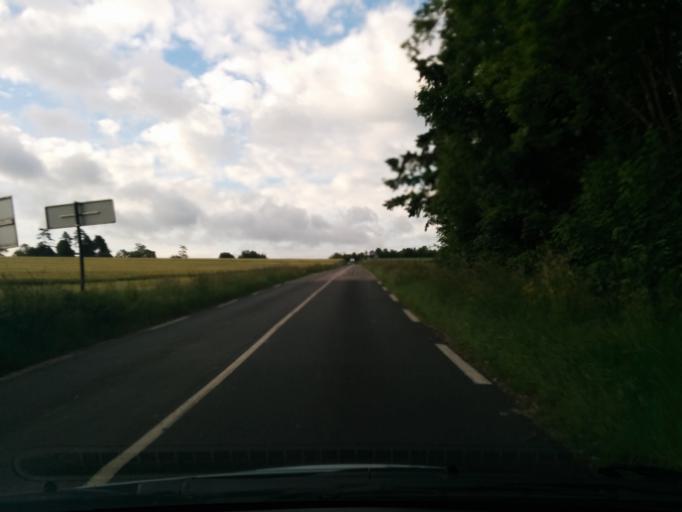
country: FR
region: Haute-Normandie
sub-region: Departement de l'Eure
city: Gasny
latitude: 49.0809
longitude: 1.6128
